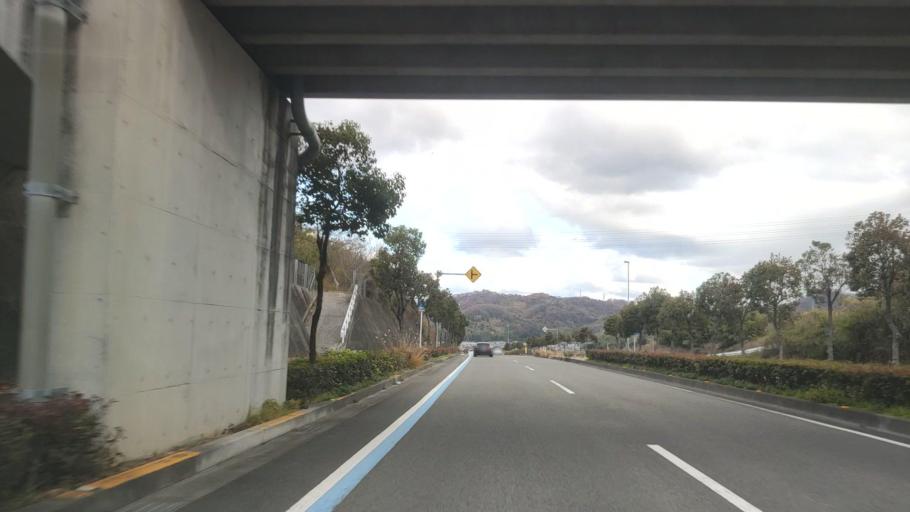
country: JP
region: Ehime
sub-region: Shikoku-chuo Shi
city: Matsuyama
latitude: 33.8911
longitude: 132.7572
